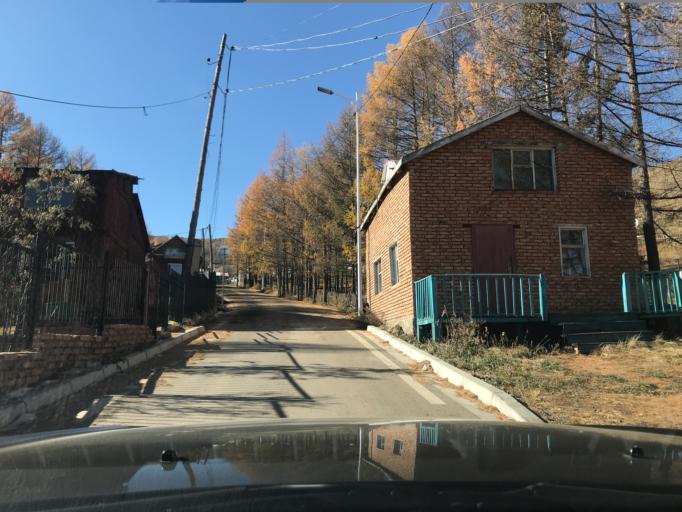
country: MN
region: Ulaanbaatar
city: Ulaanbaatar
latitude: 48.0385
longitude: 106.8889
